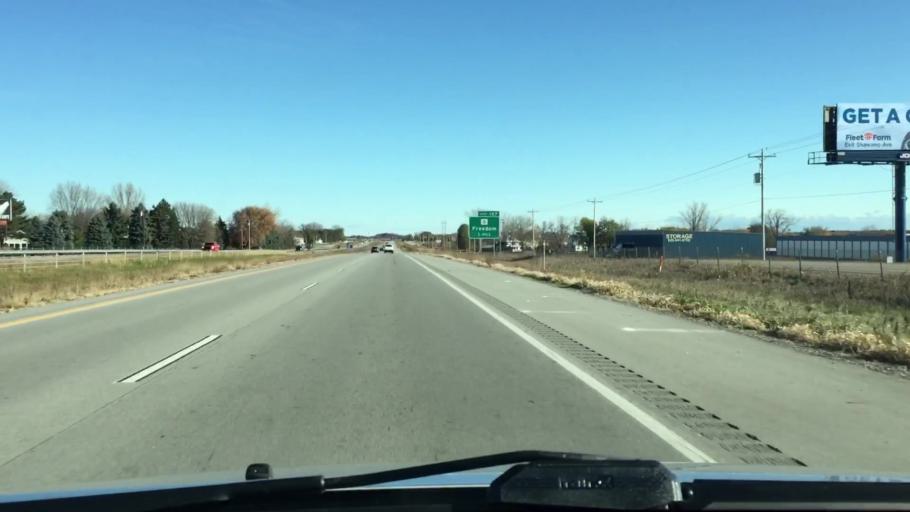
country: US
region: Wisconsin
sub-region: Brown County
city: Wrightstown
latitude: 44.3687
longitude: -88.1758
